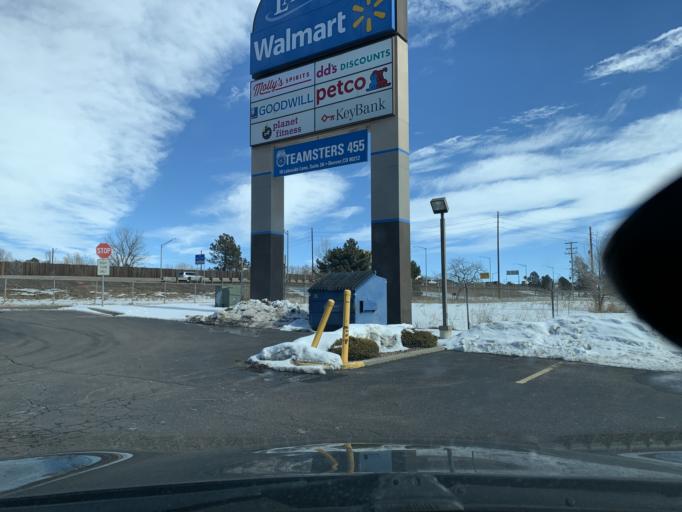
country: US
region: Colorado
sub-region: Jefferson County
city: Wheat Ridge
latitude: 39.7826
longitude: -105.0578
